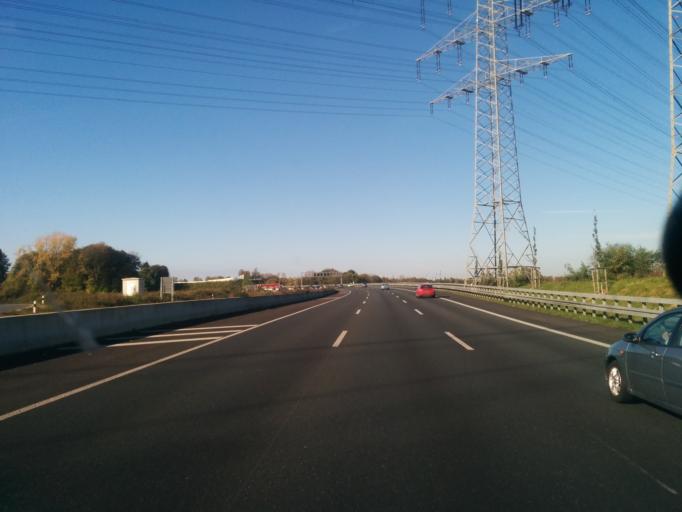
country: DE
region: North Rhine-Westphalia
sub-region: Regierungsbezirk Munster
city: Gelsenkirchen
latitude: 51.4719
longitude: 7.1074
